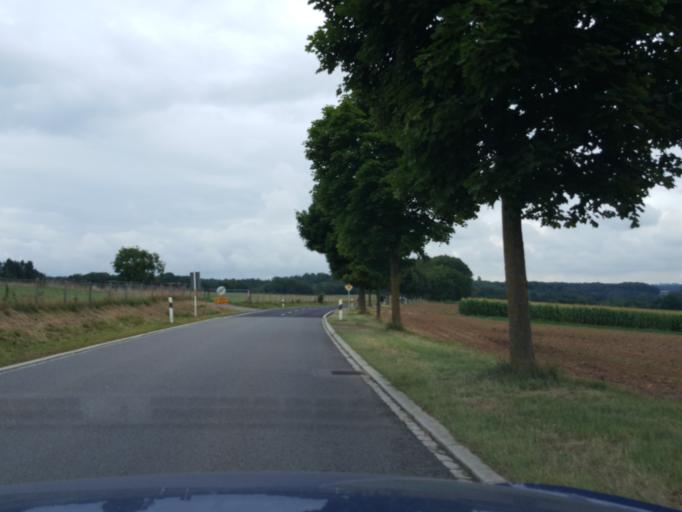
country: LU
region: Luxembourg
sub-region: Canton de Capellen
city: Kehlen
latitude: 49.6621
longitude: 6.0356
